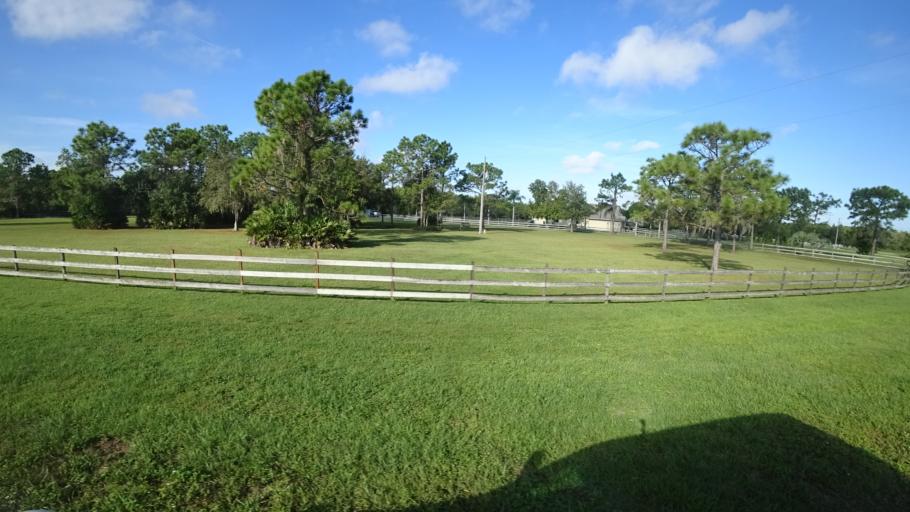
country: US
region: Florida
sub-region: Sarasota County
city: The Meadows
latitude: 27.4231
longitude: -82.3327
